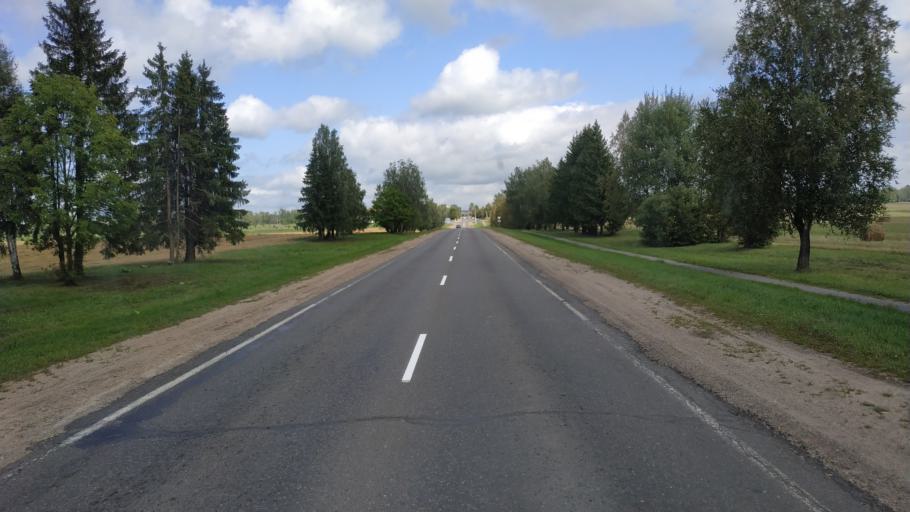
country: BY
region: Mogilev
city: Chavusy
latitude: 53.7983
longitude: 30.9484
